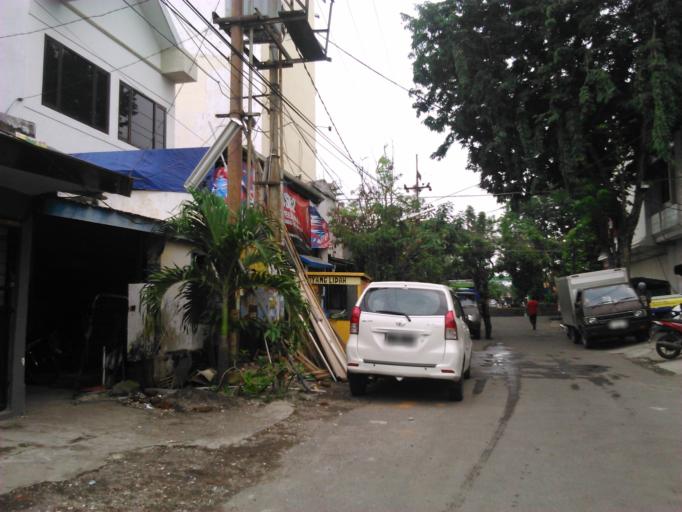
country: ID
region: East Java
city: Gubengairlangga
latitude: -7.2783
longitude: 112.7593
